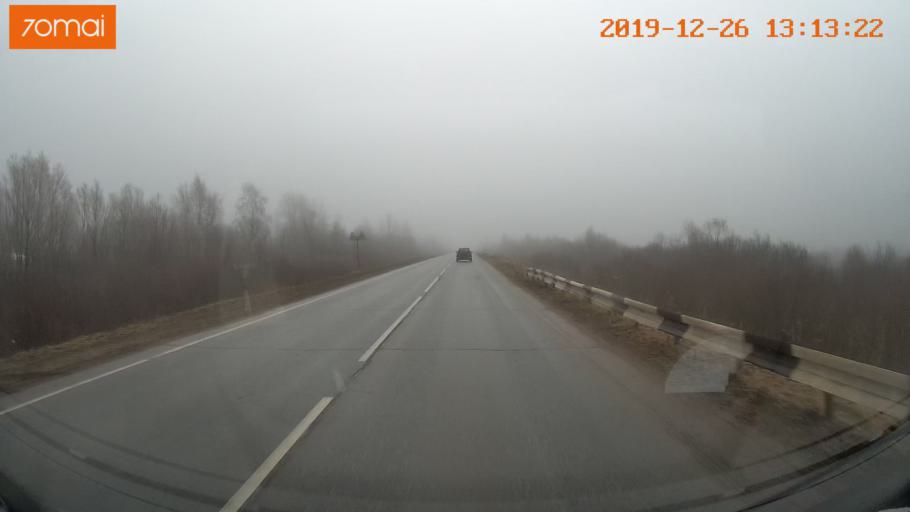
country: RU
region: Vologda
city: Cherepovets
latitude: 59.0185
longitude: 38.0511
